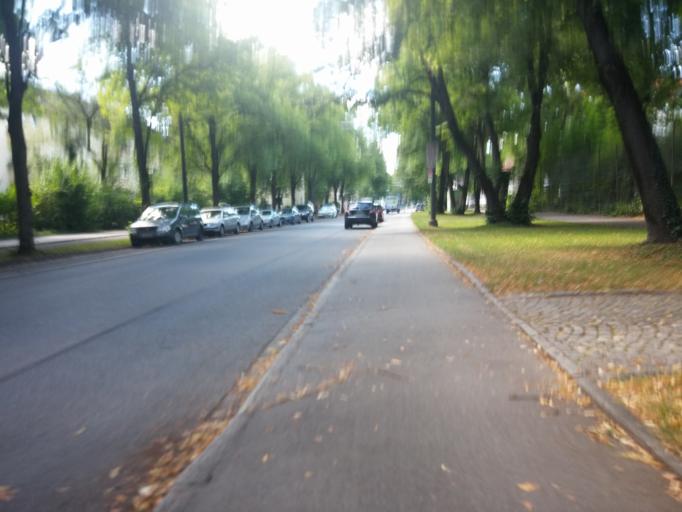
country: DE
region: Bavaria
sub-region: Upper Bavaria
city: Bogenhausen
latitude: 48.1497
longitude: 11.6120
